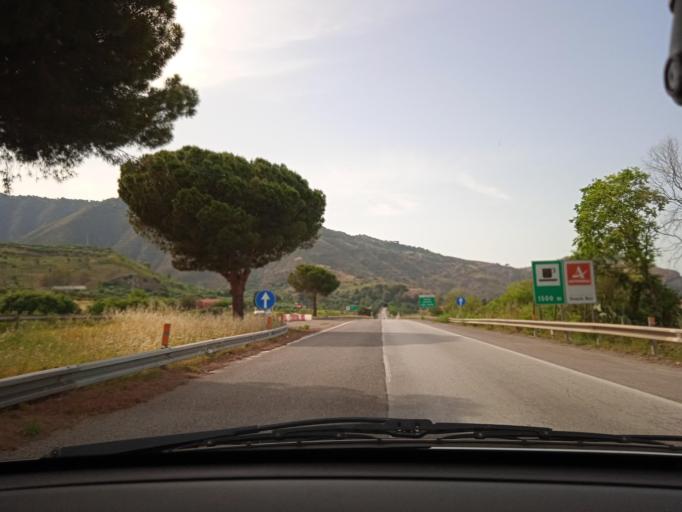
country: IT
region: Sicily
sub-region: Messina
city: Oliveri
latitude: 38.1155
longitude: 15.0653
